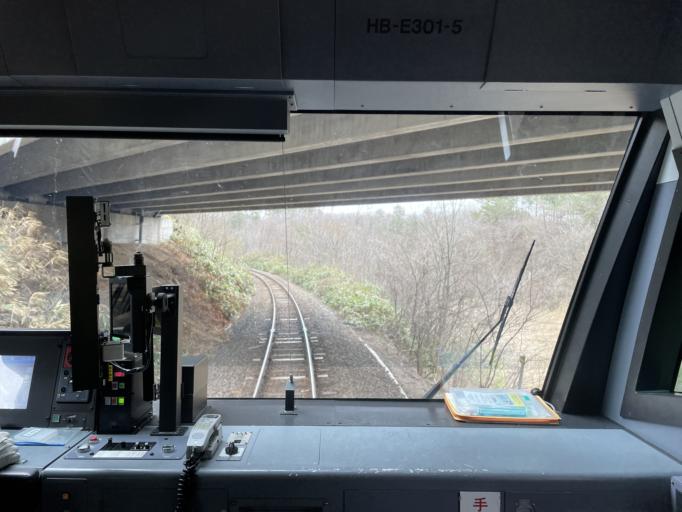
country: JP
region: Aomori
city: Shimokizukuri
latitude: 40.7742
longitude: 140.2035
